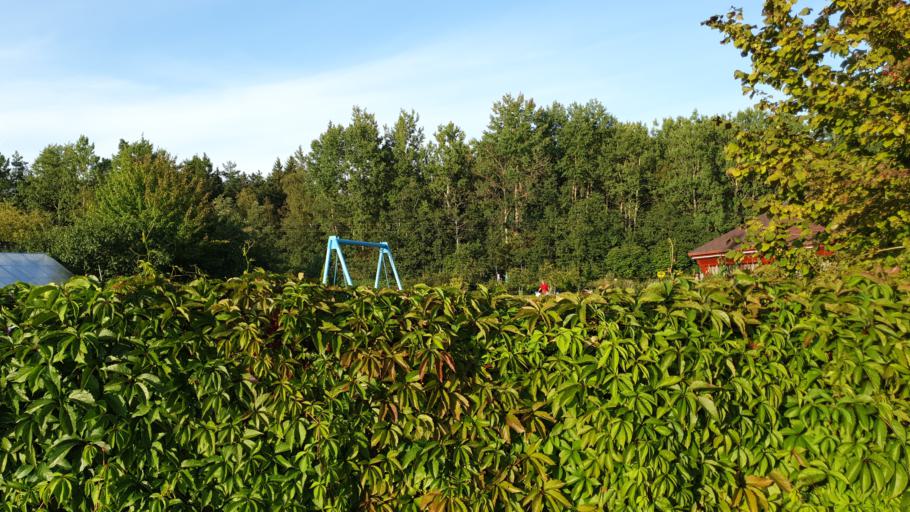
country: RU
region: Leningrad
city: Ivangorod
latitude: 59.4272
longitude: 28.3275
